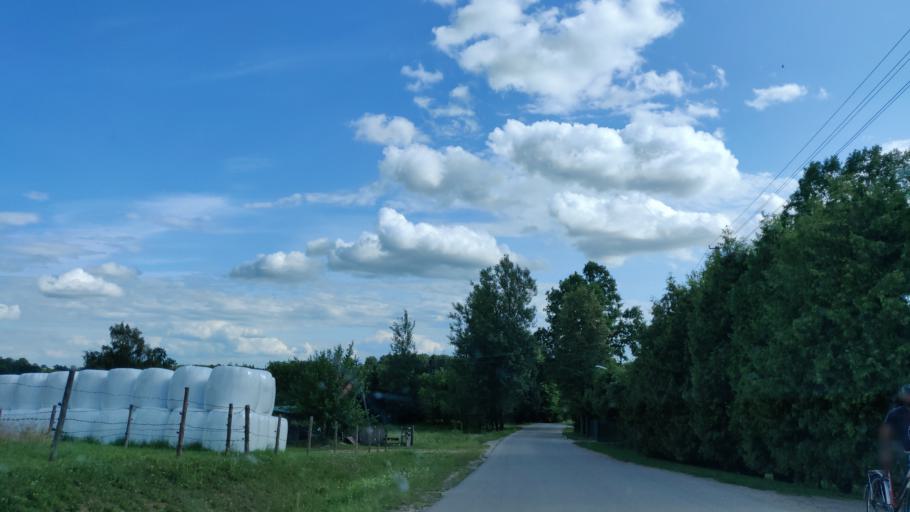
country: LT
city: Varniai
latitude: 55.5973
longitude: 22.3108
